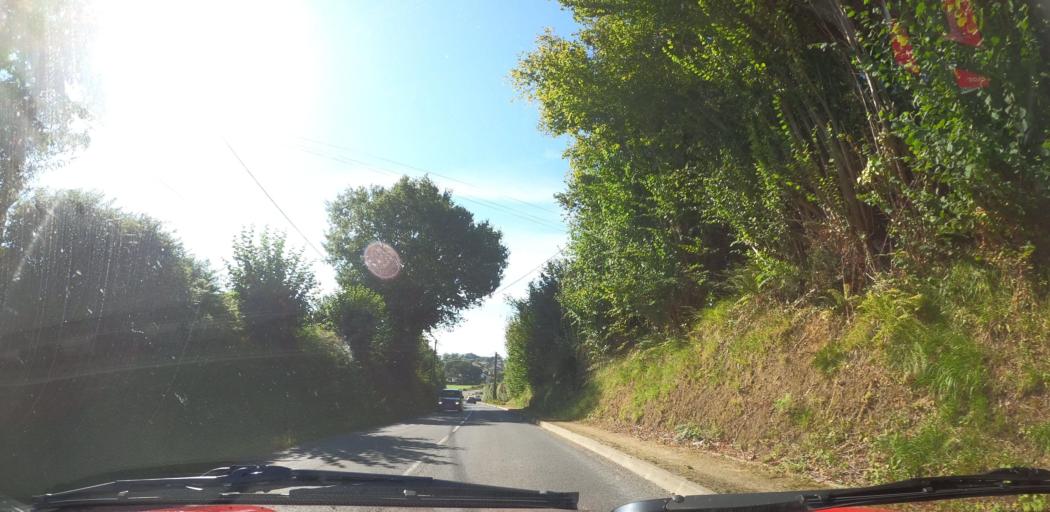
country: FR
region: Aquitaine
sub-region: Departement des Pyrenees-Atlantiques
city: Arbonne
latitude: 43.4161
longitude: -1.5487
